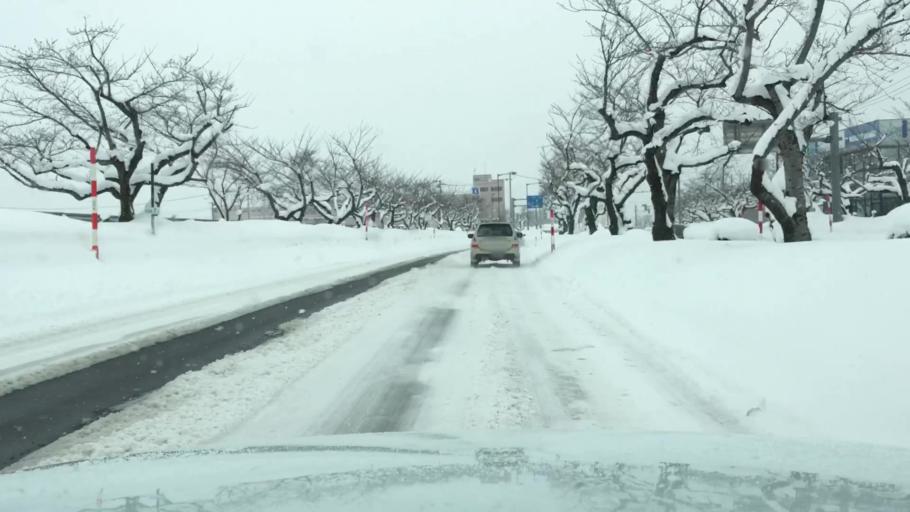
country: JP
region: Aomori
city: Hirosaki
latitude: 40.6390
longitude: 140.4892
